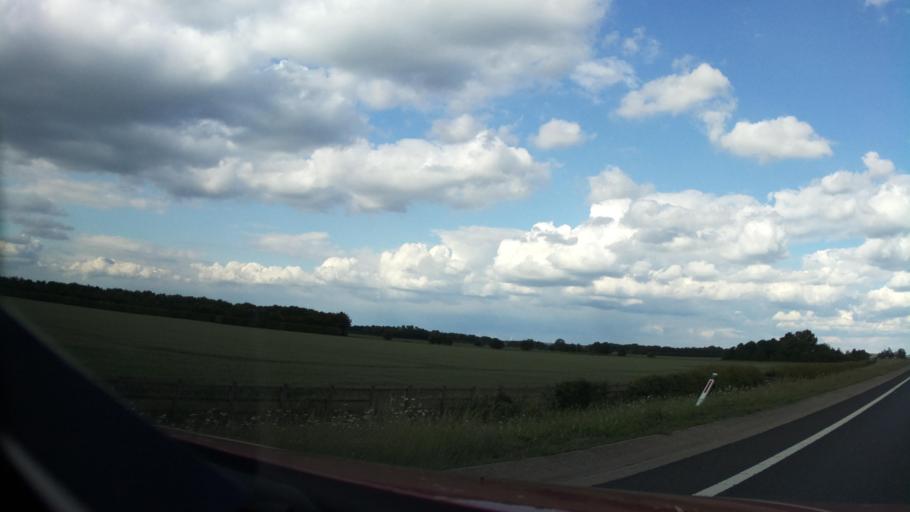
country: GB
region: England
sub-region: Bedford
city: Great Barford
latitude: 52.1682
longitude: -0.3464
